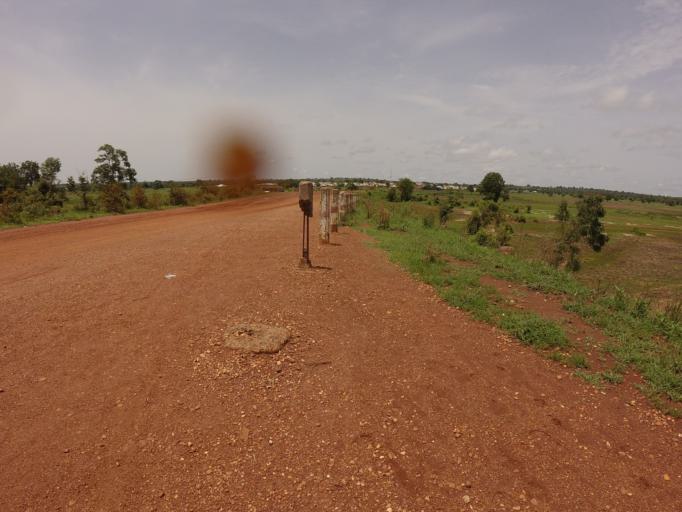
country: GH
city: Kpandae
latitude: 8.7010
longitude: 0.1718
